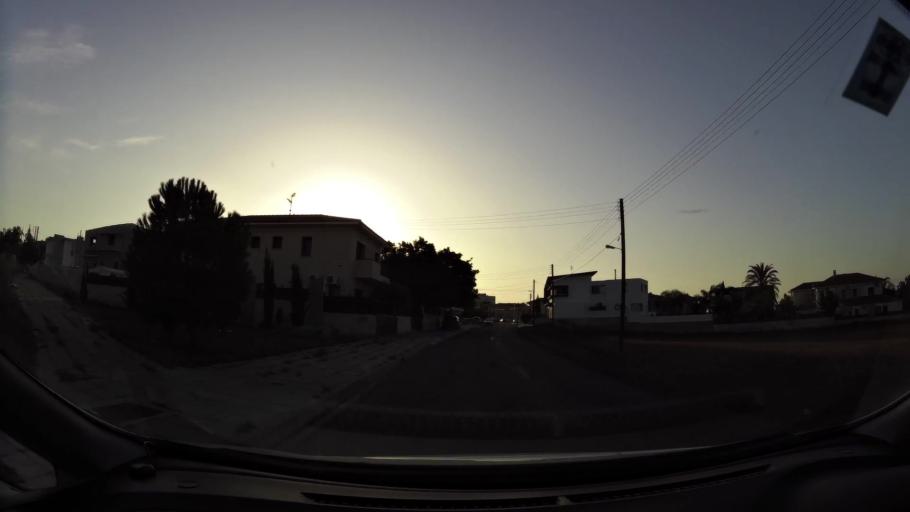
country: CY
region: Larnaka
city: Aradippou
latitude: 34.9253
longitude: 33.5866
